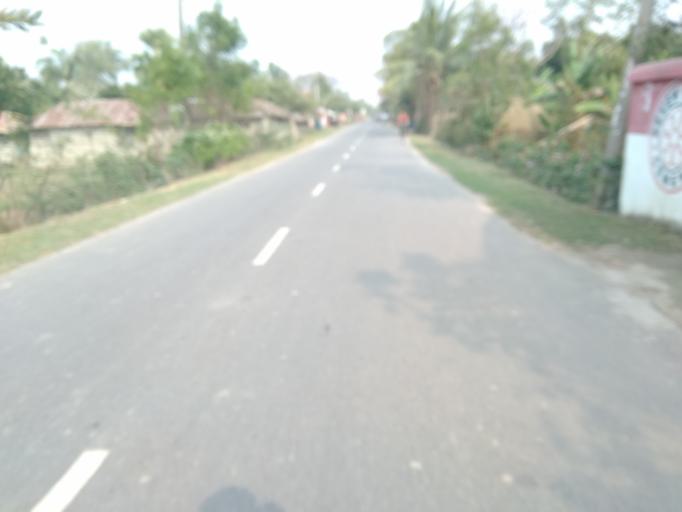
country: IN
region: West Bengal
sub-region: North 24 Parganas
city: Taki
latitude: 22.3469
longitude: 89.1943
